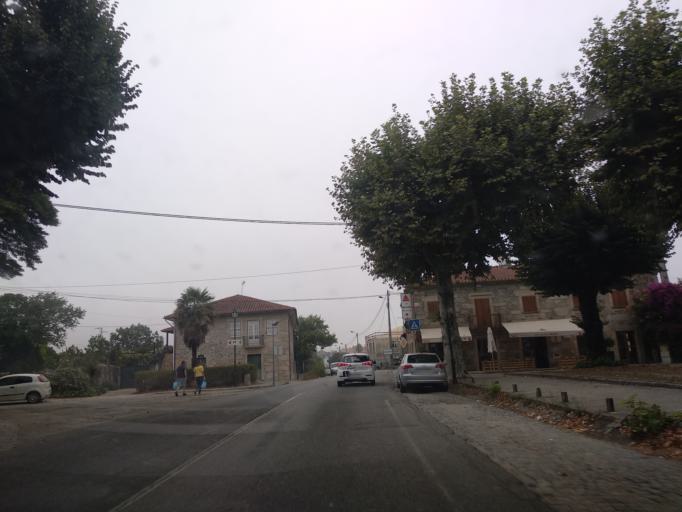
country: PT
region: Braga
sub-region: Vila Verde
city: Vila Verde
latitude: 41.6272
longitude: -8.4334
